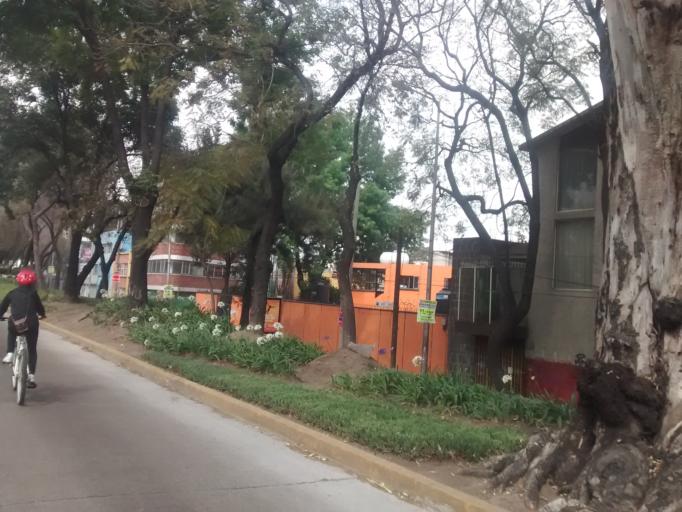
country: MX
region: Mexico City
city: Coyoacan
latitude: 19.3581
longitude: -99.1598
